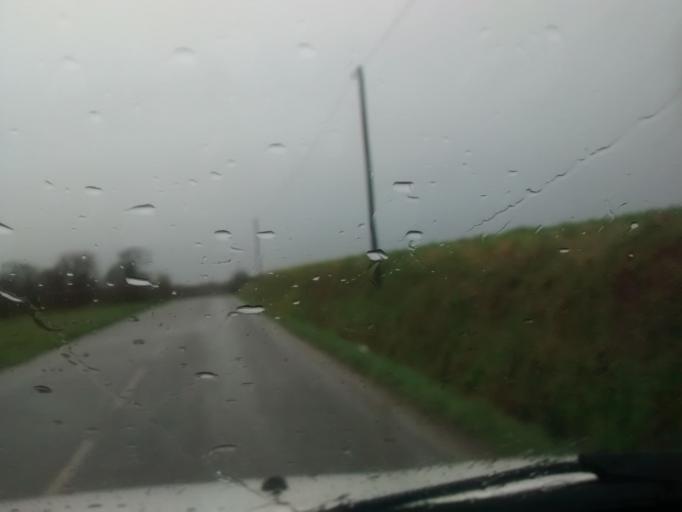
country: FR
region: Brittany
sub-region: Departement d'Ille-et-Vilaine
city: Saint-Pere
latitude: 48.5740
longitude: -1.9001
